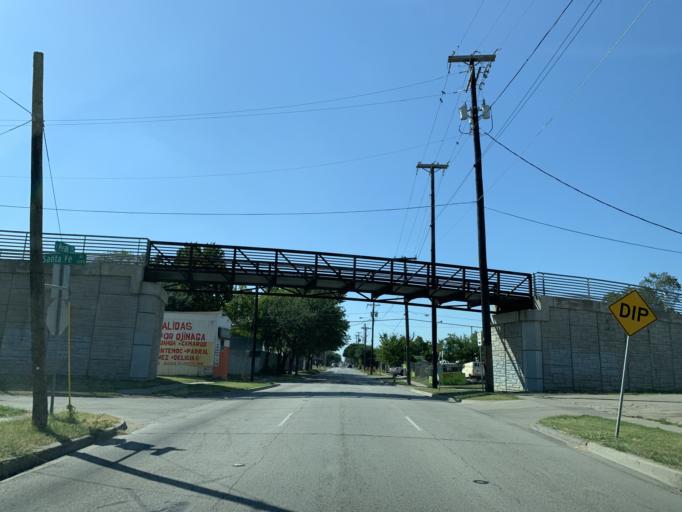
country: US
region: Texas
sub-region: Dallas County
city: Dallas
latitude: 32.7882
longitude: -96.7670
